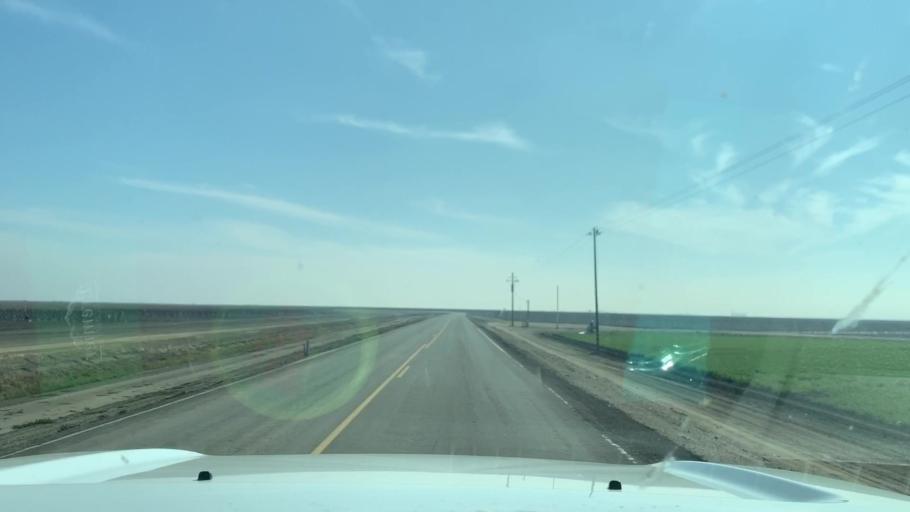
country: US
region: California
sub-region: Kern County
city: Buttonwillow
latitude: 35.4573
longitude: -119.5749
